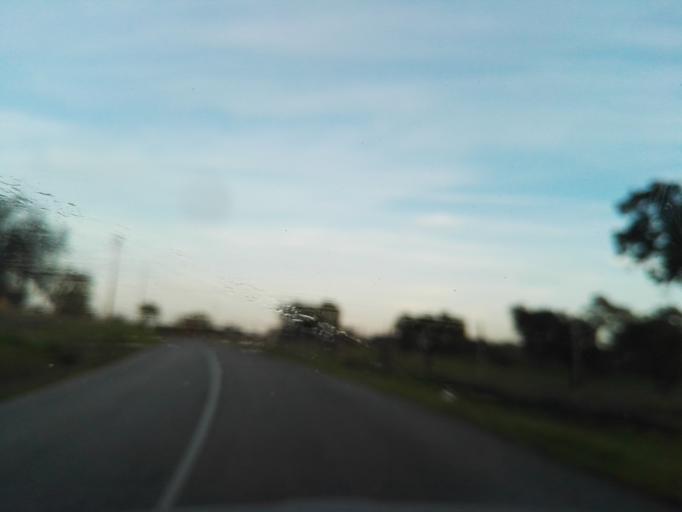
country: PT
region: Evora
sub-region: Montemor-O-Novo
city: Montemor-o-Novo
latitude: 38.7783
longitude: -8.2125
